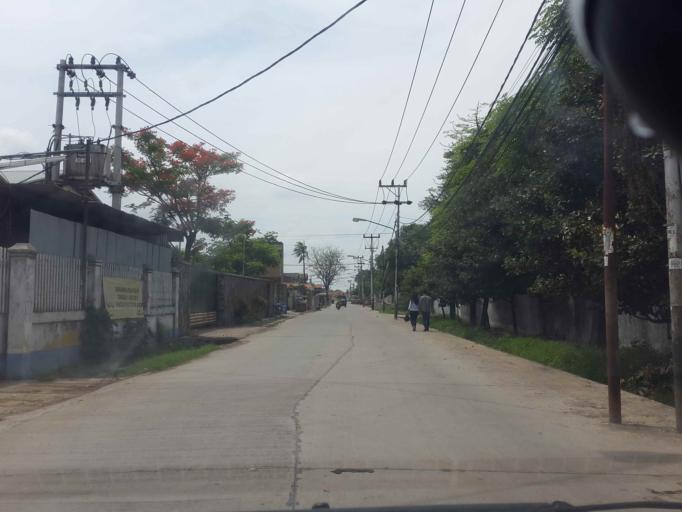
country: ID
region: West Java
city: Teluknaga
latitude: -6.1249
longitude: 106.6202
